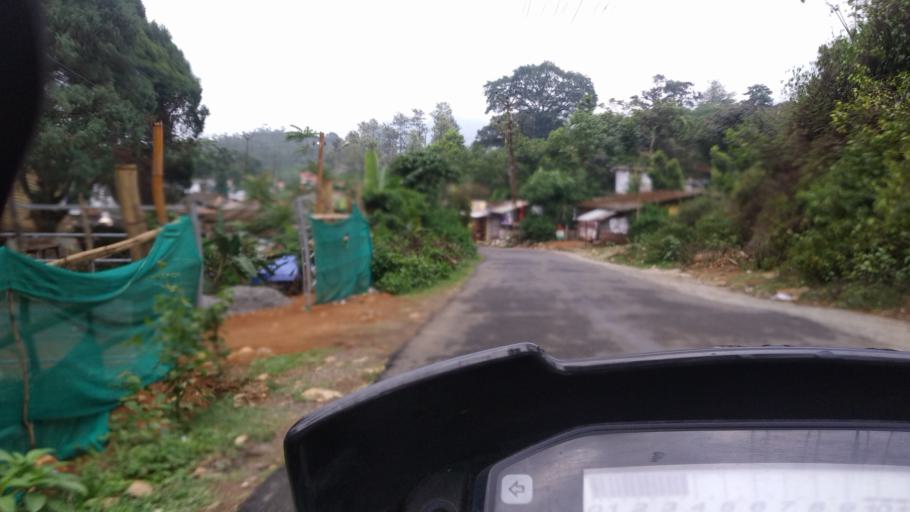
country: IN
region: Kerala
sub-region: Kottayam
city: Erattupetta
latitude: 9.6345
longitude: 76.9547
